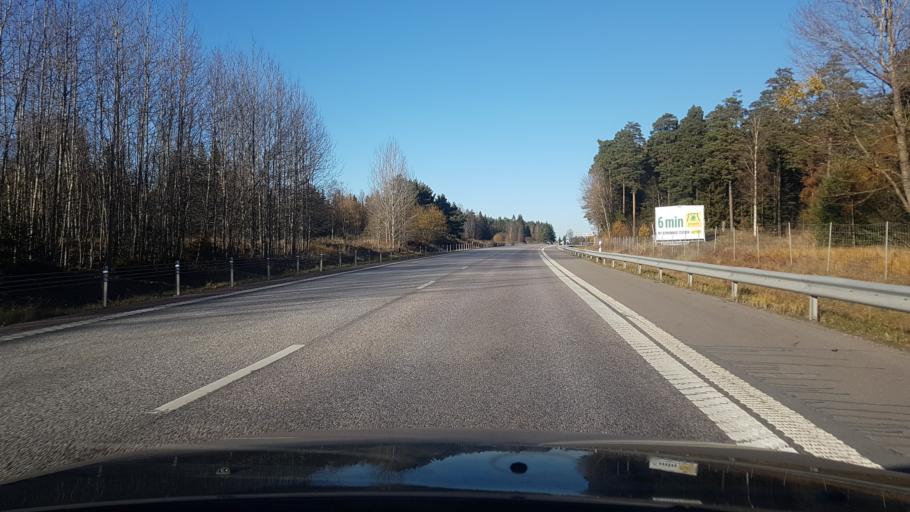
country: SE
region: Uppsala
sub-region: Uppsala Kommun
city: Alsike
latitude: 59.7889
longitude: 17.7762
